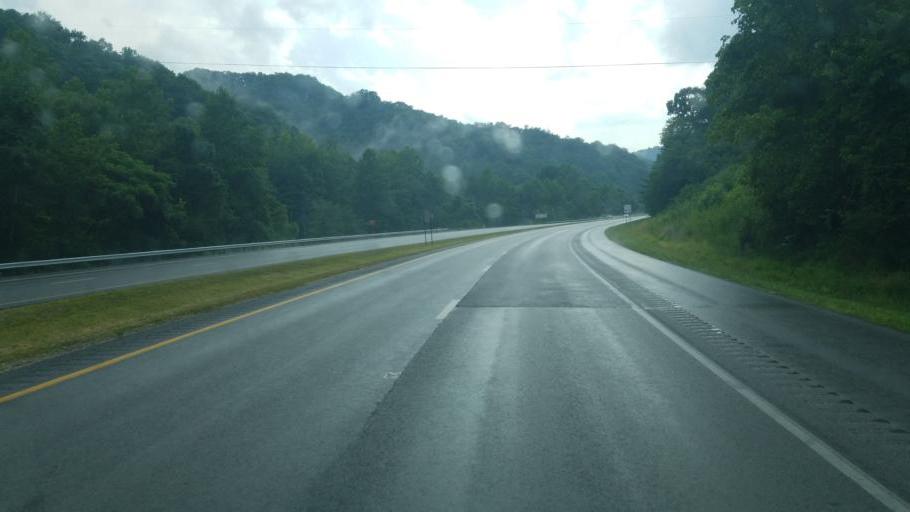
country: US
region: West Virginia
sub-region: Logan County
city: Chapmanville
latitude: 37.9883
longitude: -81.9356
